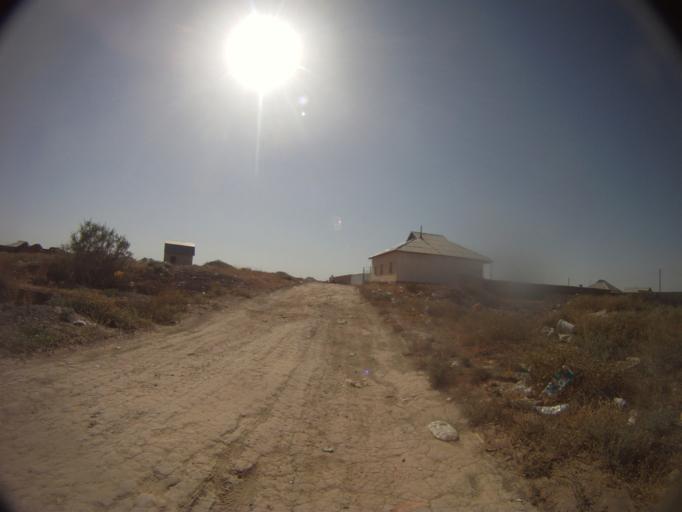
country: KZ
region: Ongtustik Qazaqstan
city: Turkestan
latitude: 43.2856
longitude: 68.2644
